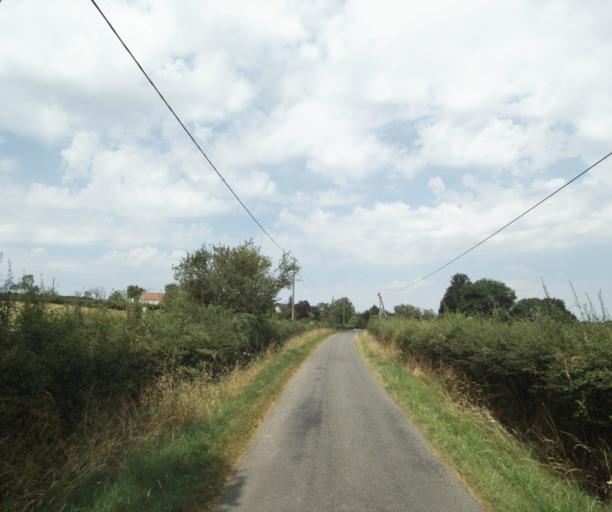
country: FR
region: Bourgogne
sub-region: Departement de Saone-et-Loire
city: Gueugnon
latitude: 46.5881
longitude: 4.0406
